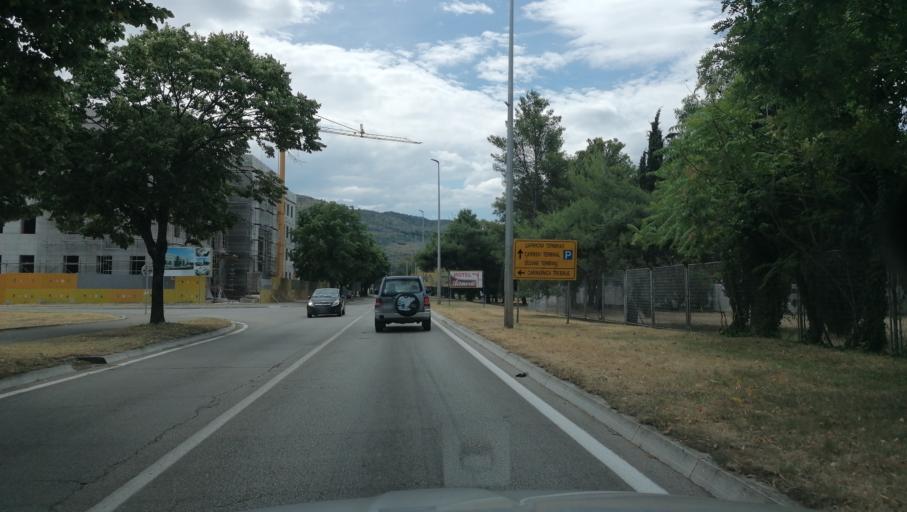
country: BA
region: Republika Srpska
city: Trebinje
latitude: 42.7083
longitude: 18.3425
